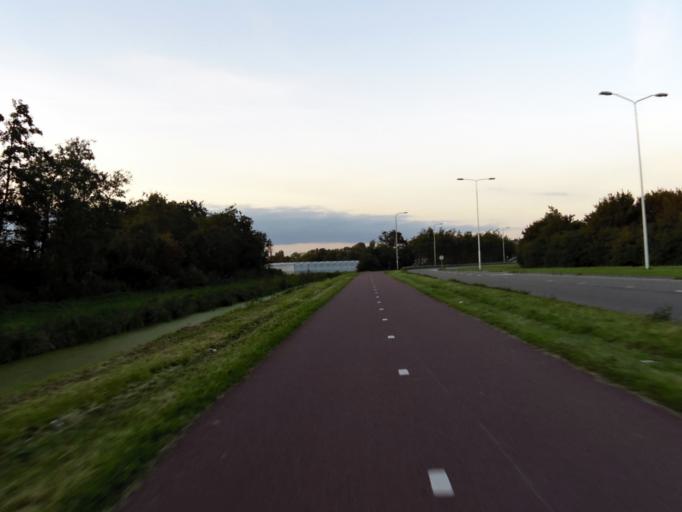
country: NL
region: South Holland
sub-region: Gemeente Voorschoten
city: Voorschoten
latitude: 52.1586
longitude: 4.4445
